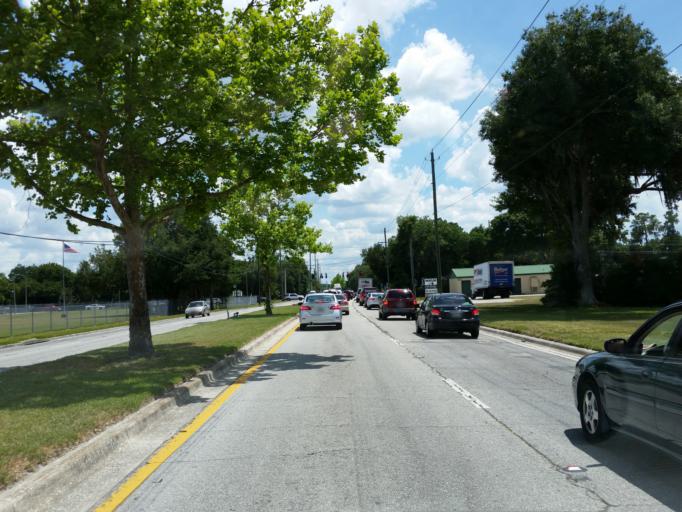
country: US
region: Florida
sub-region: Hillsborough County
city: Plant City
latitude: 28.0056
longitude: -82.1378
